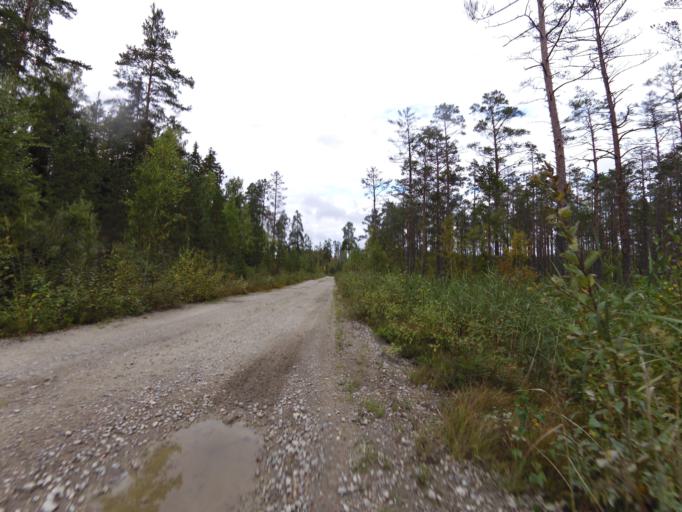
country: SE
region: Gaevleborg
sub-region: Gavle Kommun
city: Valbo
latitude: 60.7426
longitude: 17.0249
